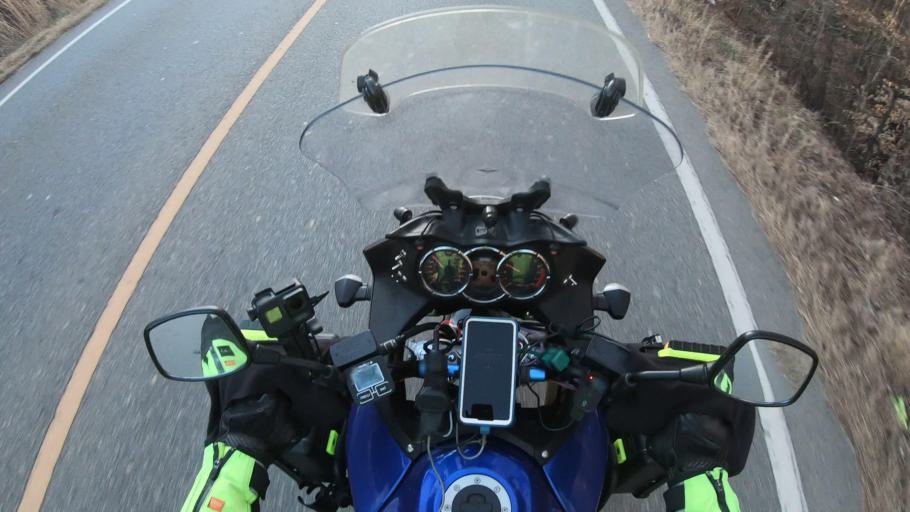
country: US
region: Georgia
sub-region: Dawson County
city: Dawsonville
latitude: 34.3539
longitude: -84.0616
